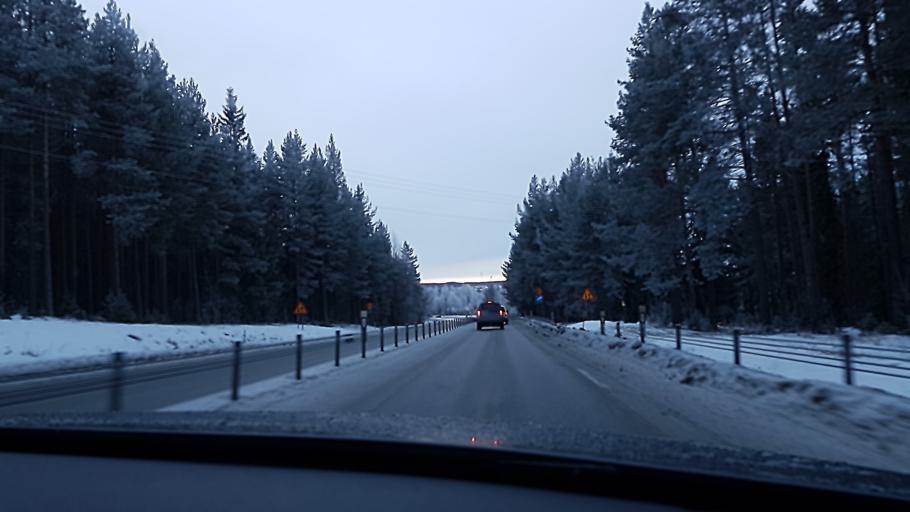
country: SE
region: Jaemtland
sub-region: OEstersunds Kommun
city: Brunflo
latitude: 63.1089
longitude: 14.7956
